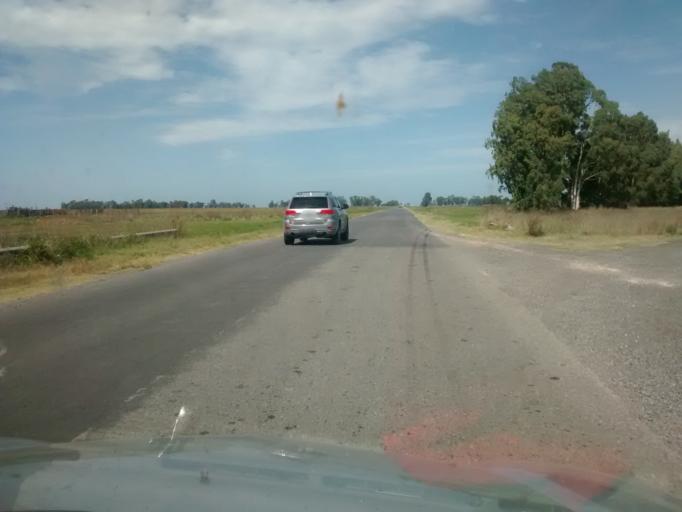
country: AR
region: Buenos Aires
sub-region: Partido de Ayacucho
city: Ayacucho
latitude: -37.2127
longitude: -58.5017
